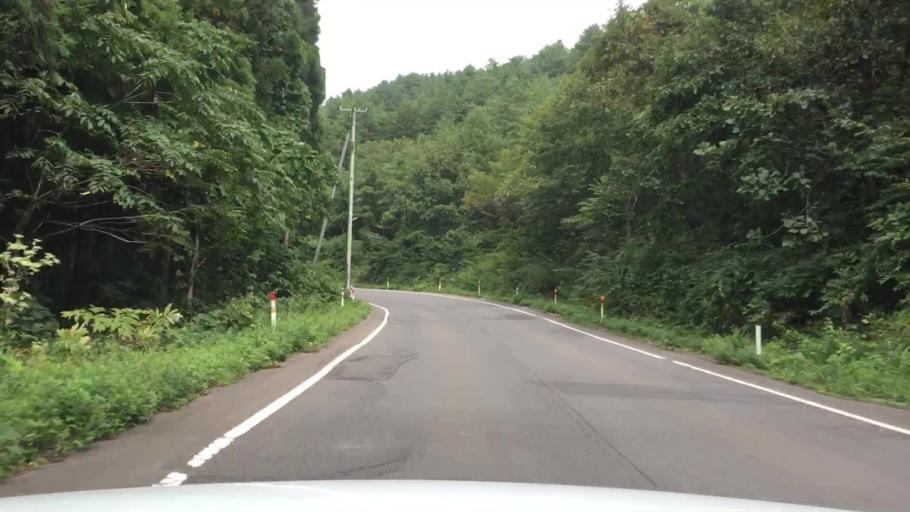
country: JP
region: Aomori
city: Shimokizukuri
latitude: 40.7215
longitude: 140.2584
